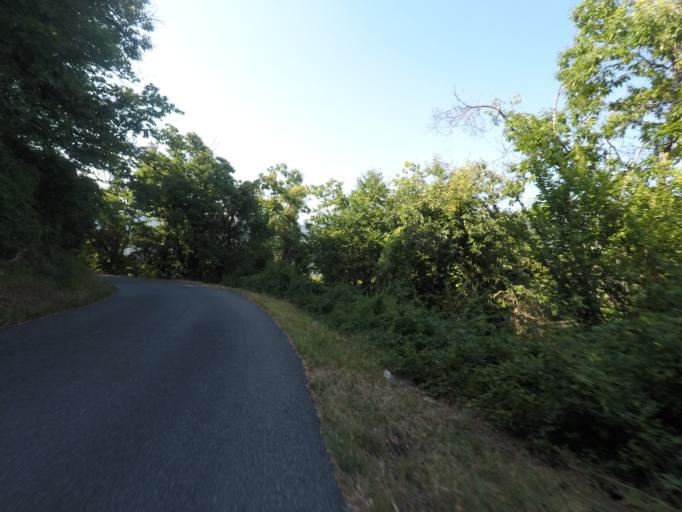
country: IT
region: Liguria
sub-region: Provincia di La Spezia
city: Casano-Dogana-Isola
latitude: 44.0873
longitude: 10.0594
